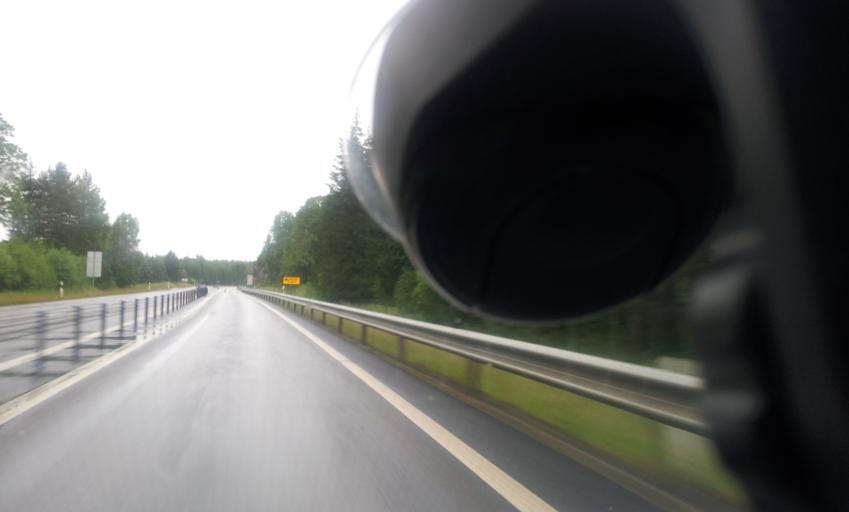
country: SE
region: OEstergoetland
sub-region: Valdemarsviks Kommun
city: Valdemarsvik
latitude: 58.1831
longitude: 16.5365
